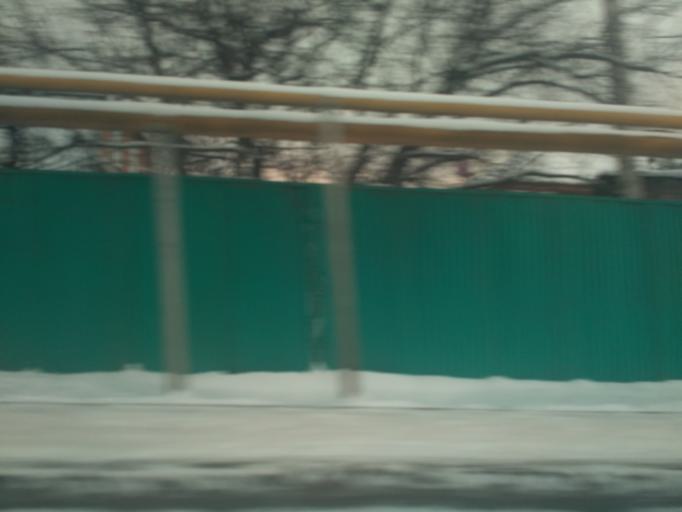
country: KZ
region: Almaty Qalasy
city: Almaty
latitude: 43.2251
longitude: 76.7953
